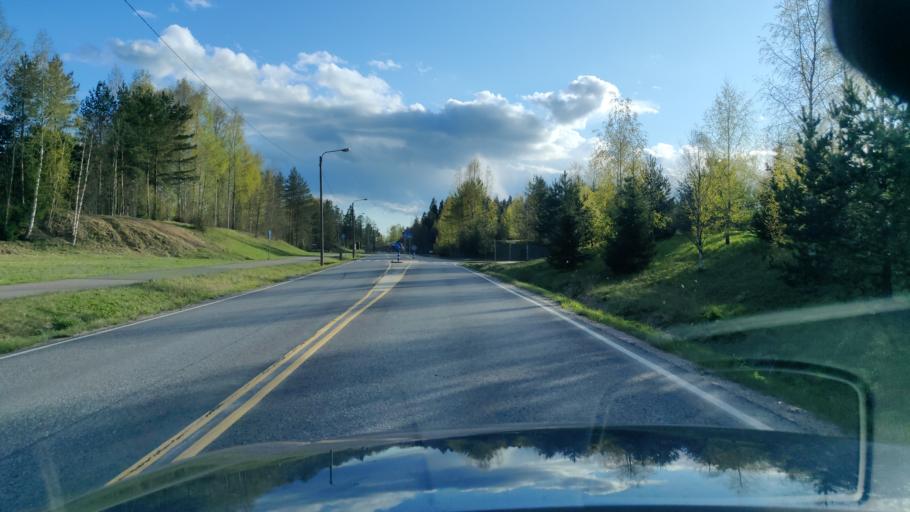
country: FI
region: Uusimaa
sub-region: Helsinki
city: Tuusula
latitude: 60.4170
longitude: 25.0084
